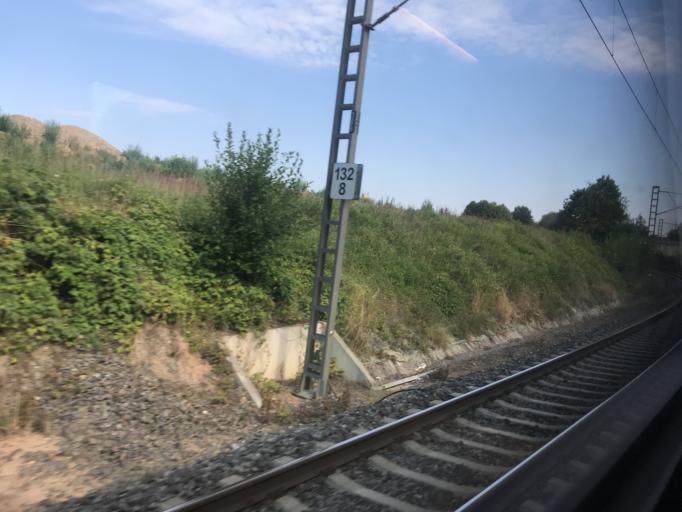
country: CZ
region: Central Bohemia
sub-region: Okres Benesov
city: Benesov
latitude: 49.7648
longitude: 14.6906
